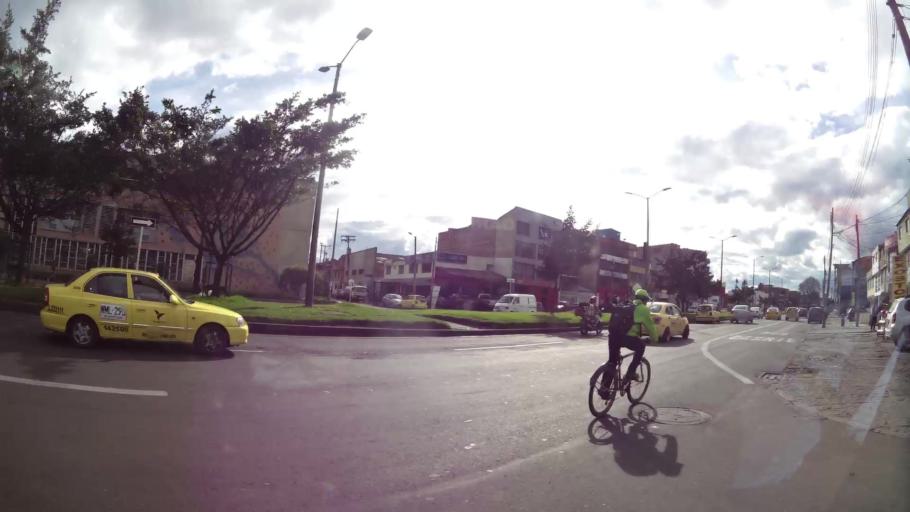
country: CO
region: Bogota D.C.
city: Bogota
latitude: 4.6040
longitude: -74.1232
